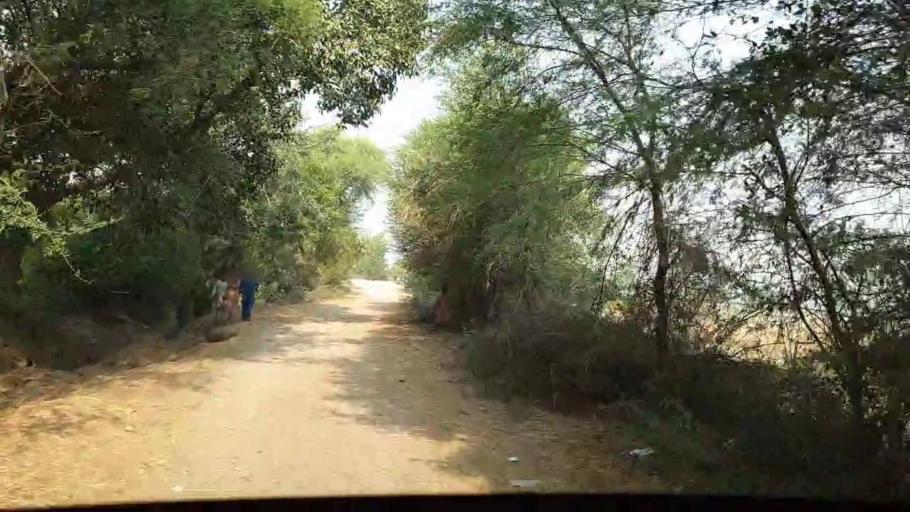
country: PK
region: Sindh
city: Chuhar Jamali
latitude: 24.5061
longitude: 68.0416
